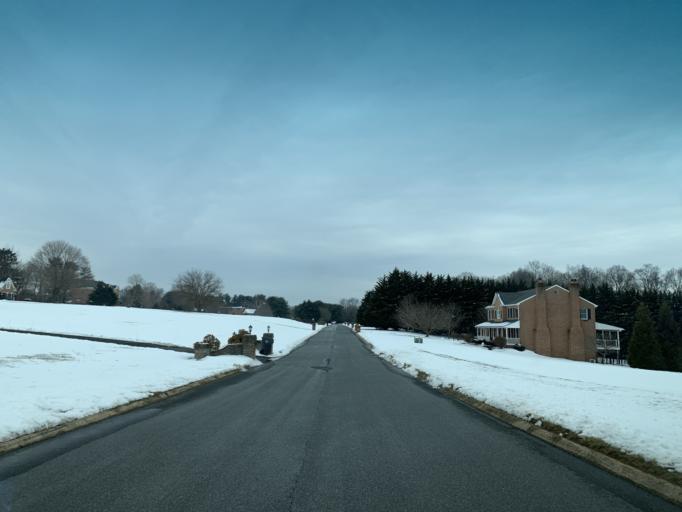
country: US
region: Maryland
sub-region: Harford County
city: Jarrettsville
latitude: 39.5842
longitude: -76.4649
